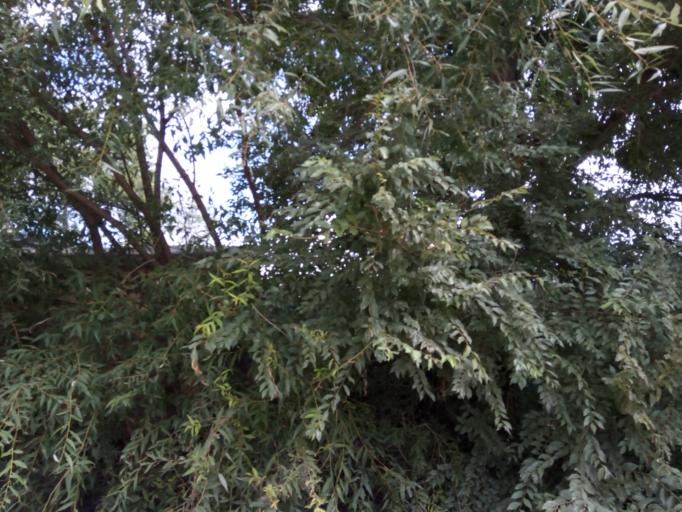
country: RU
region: Primorskiy
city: Dal'nerechensk
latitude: 45.9415
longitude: 133.8103
